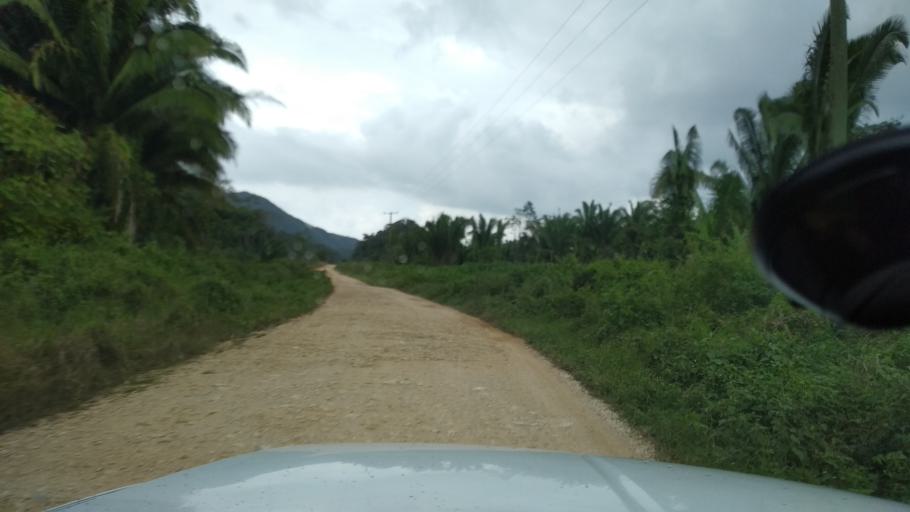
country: BZ
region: Toledo
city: Punta Gorda
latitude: 16.2026
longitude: -89.0345
